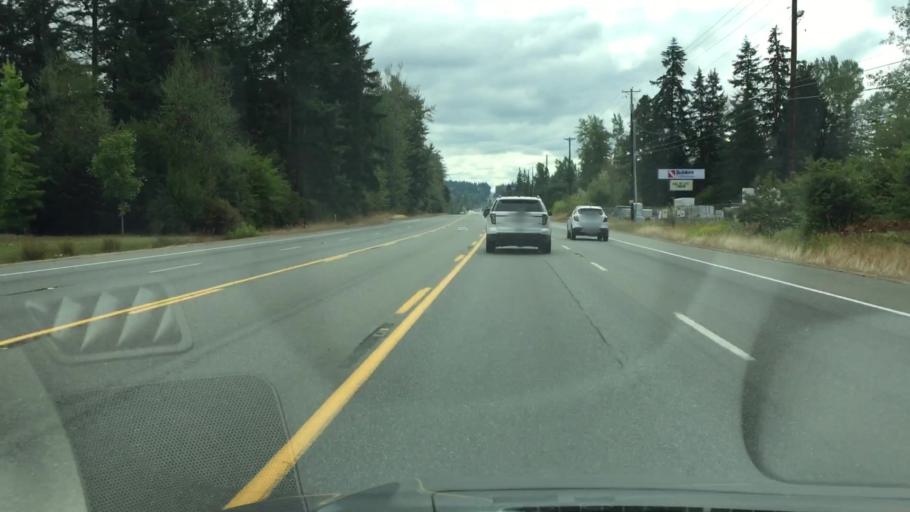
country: US
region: Washington
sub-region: Pierce County
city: Graham
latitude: 47.0681
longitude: -122.2947
